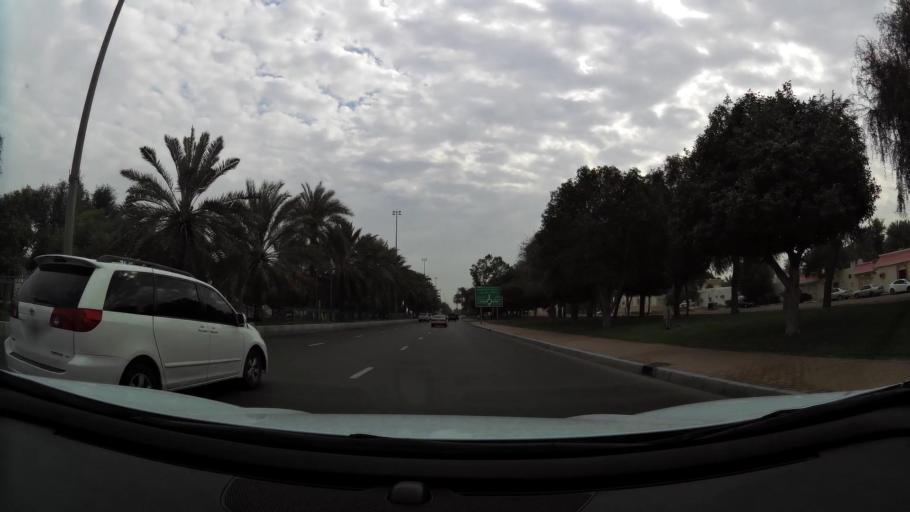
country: AE
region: Abu Dhabi
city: Al Ain
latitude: 24.2243
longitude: 55.7422
